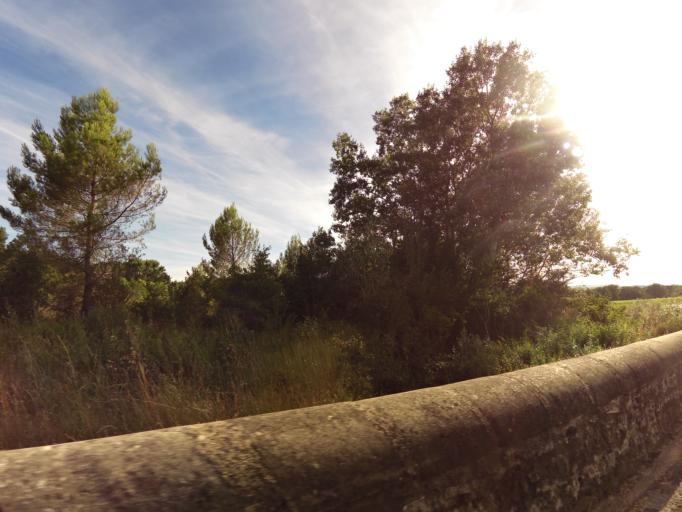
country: FR
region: Languedoc-Roussillon
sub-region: Departement du Gard
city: Villevieille
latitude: 43.8232
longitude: 4.1338
